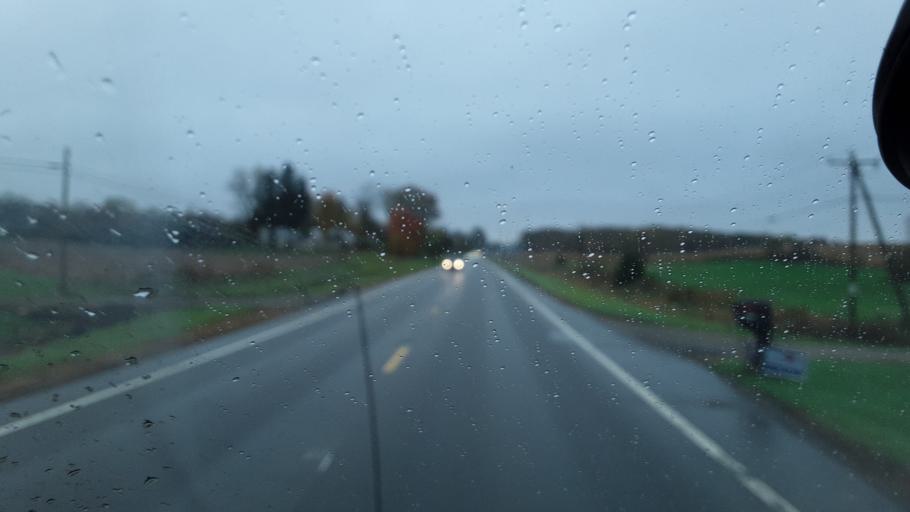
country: US
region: Ohio
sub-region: Morrow County
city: Mount Gilead
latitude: 40.5126
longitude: -82.7377
